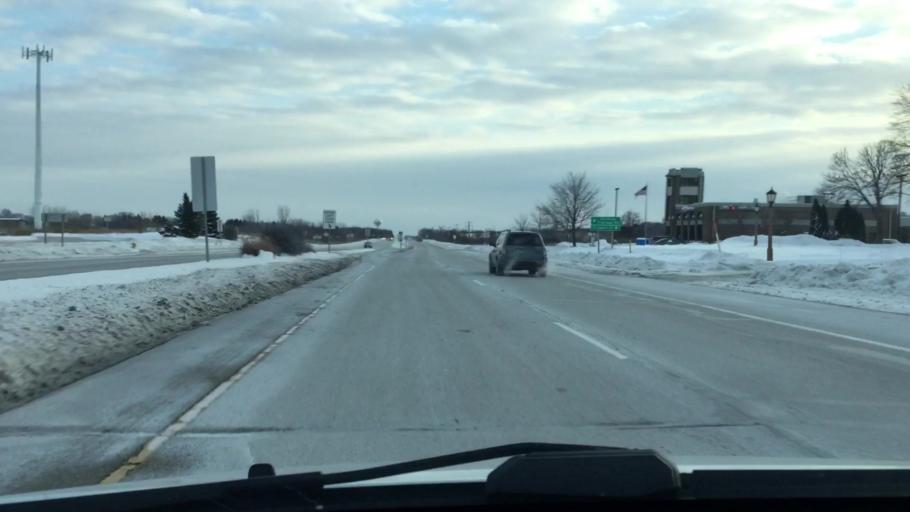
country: US
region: Wisconsin
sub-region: Waukesha County
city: Sussex
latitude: 43.1361
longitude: -88.2440
